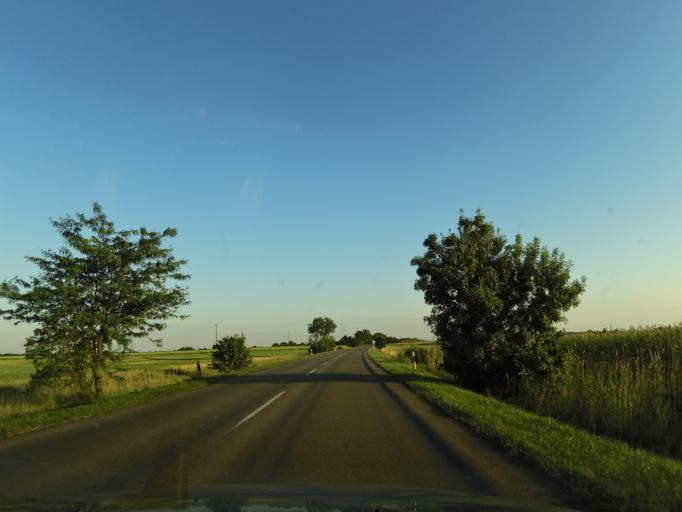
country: HU
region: Csongrad
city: Szegvar
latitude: 46.5450
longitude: 20.3171
